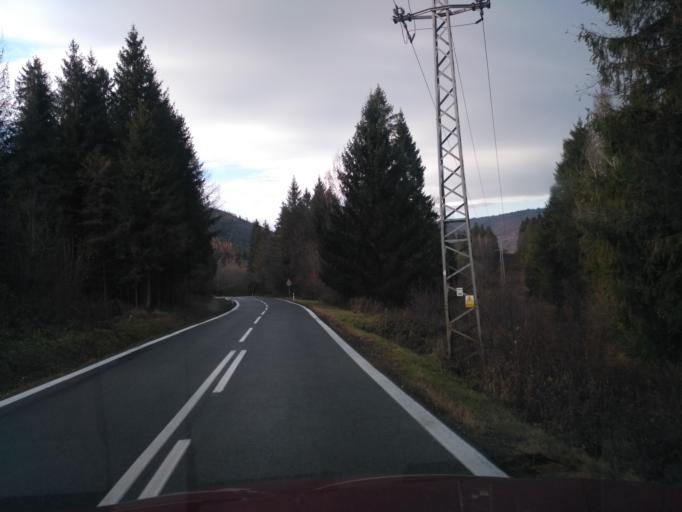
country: SK
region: Kosicky
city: Spisska Nova Ves
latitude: 48.8157
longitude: 20.6665
